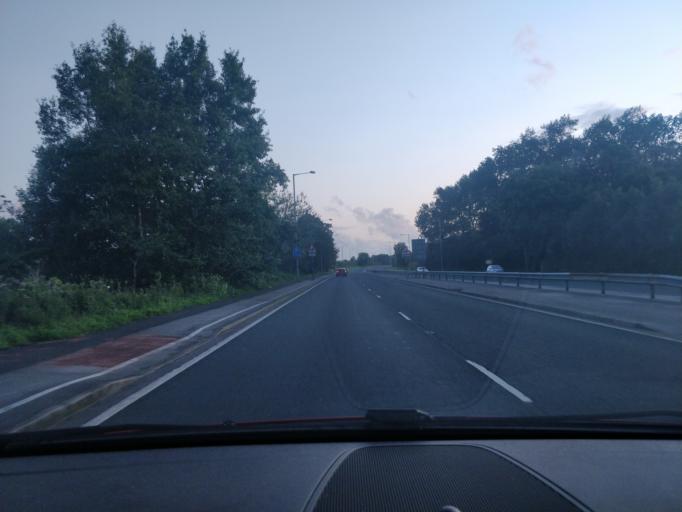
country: GB
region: England
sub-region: Lancashire
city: Croston
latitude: 53.7114
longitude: -2.7810
